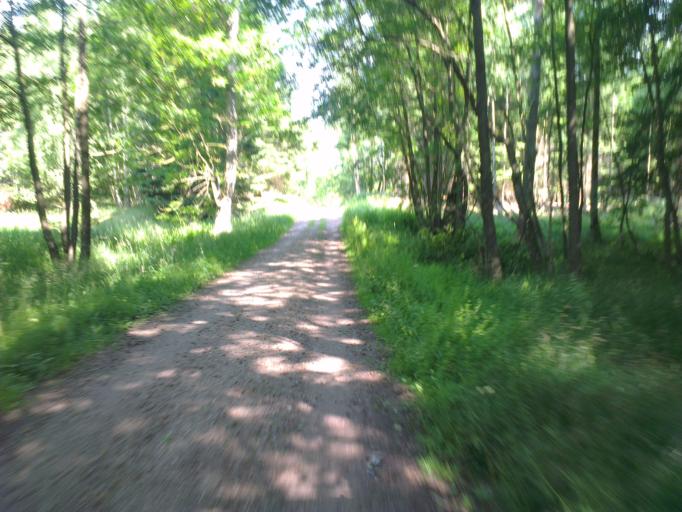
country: DK
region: Capital Region
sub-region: Allerod Kommune
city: Lillerod
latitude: 55.9246
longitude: 12.3617
